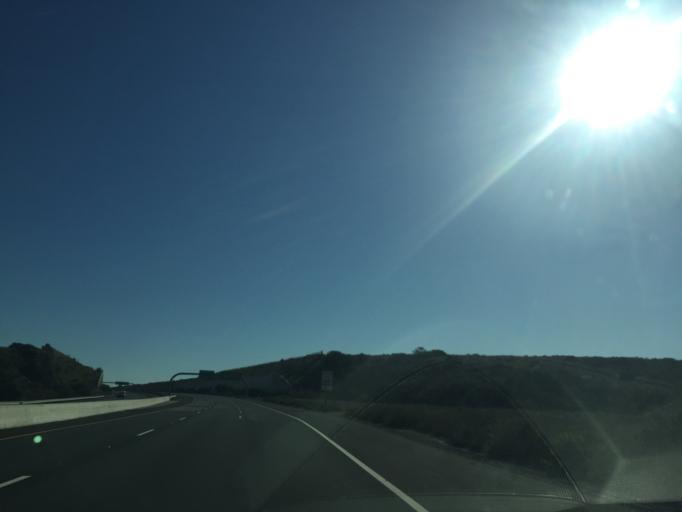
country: MX
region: Baja California
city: Tijuana
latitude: 32.5861
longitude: -116.9657
